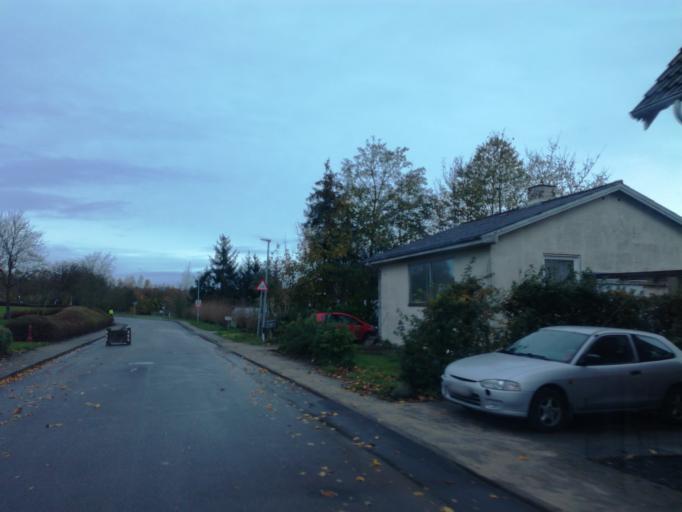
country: DK
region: South Denmark
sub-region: Vejle Kommune
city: Borkop
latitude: 55.6456
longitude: 9.6468
